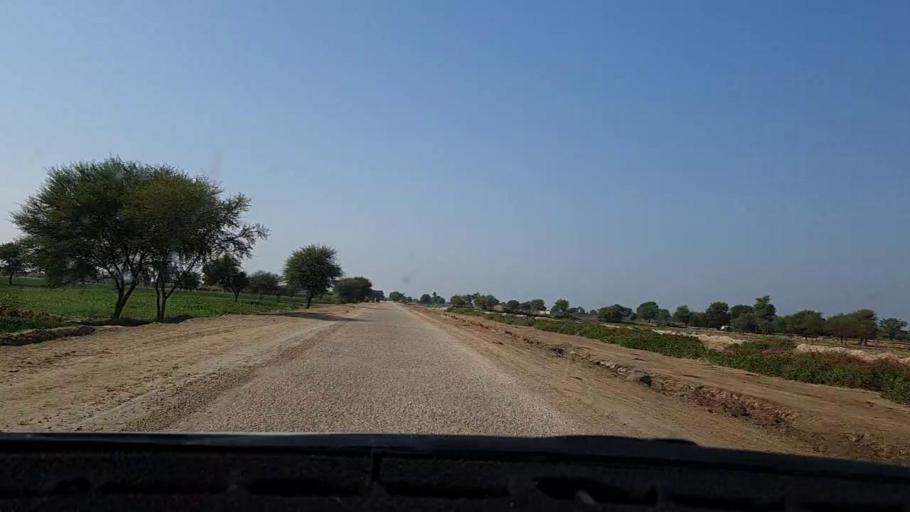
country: PK
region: Sindh
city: Tando Mittha Khan
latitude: 25.8064
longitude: 69.3288
